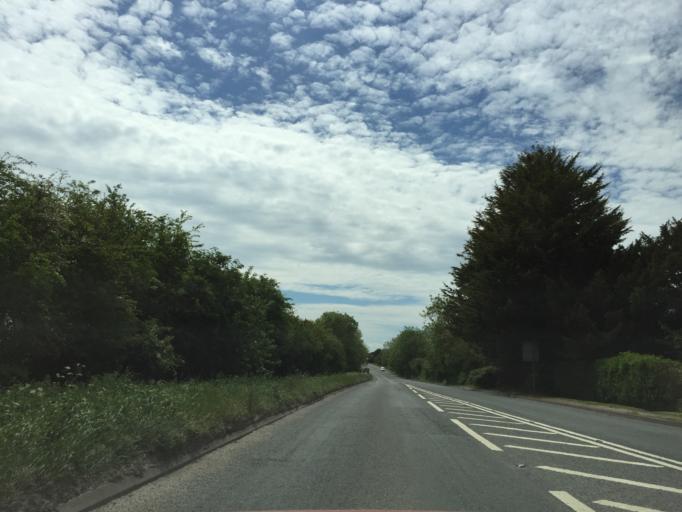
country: GB
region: England
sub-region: Gloucestershire
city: Stonehouse
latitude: 51.7806
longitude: -2.3171
